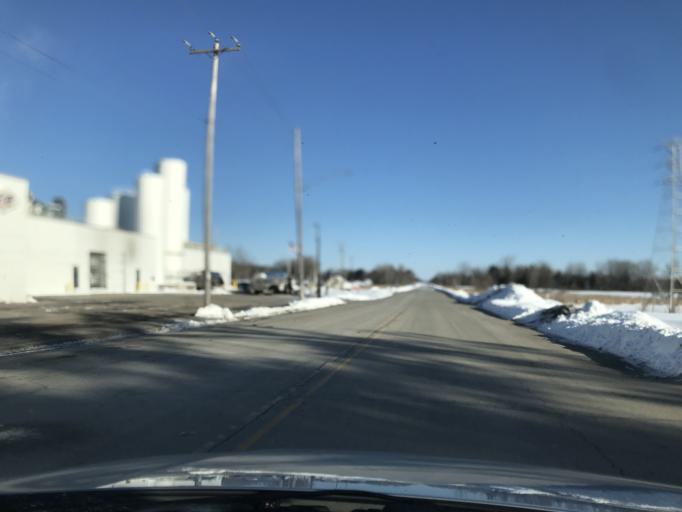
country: US
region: Wisconsin
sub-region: Oconto County
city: Oconto Falls
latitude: 44.9543
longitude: -88.0467
